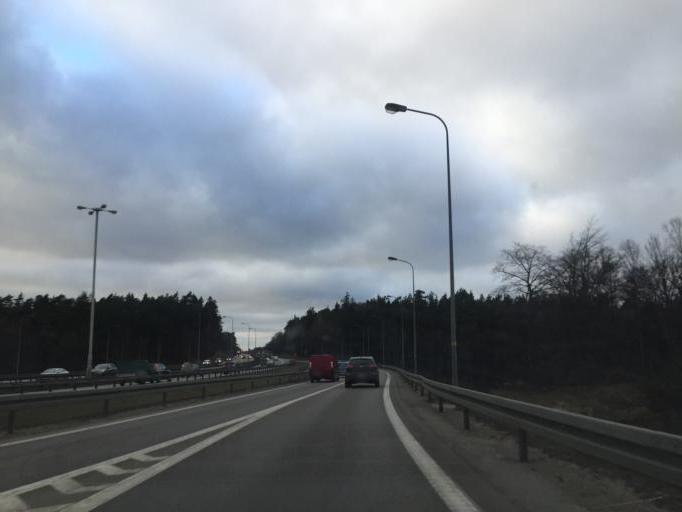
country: PL
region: Pomeranian Voivodeship
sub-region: Sopot
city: Sopot
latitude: 54.3788
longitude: 18.5126
